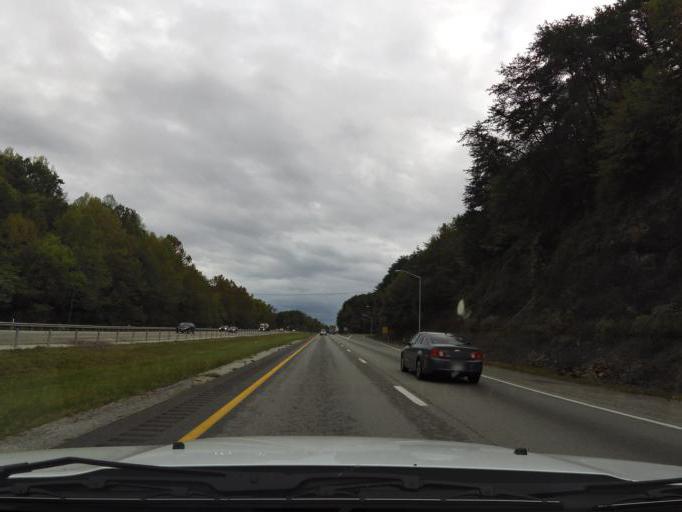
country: US
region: Kentucky
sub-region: Whitley County
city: Williamsburg
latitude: 36.7868
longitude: -84.1701
